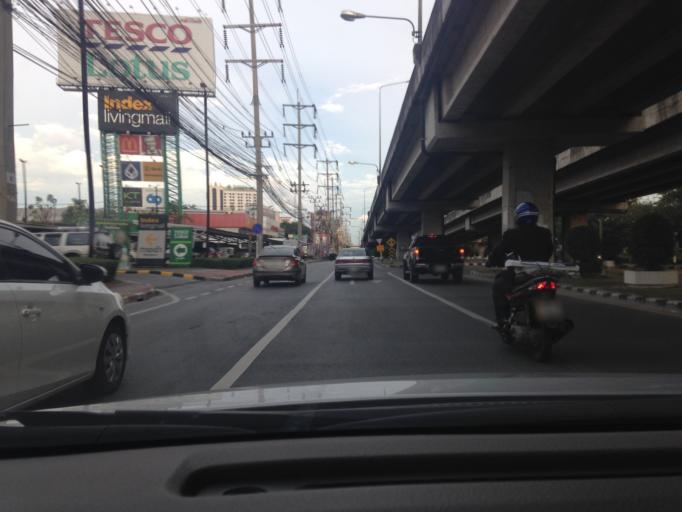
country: TH
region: Bangkok
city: Lak Si
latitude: 13.8950
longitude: 100.5555
